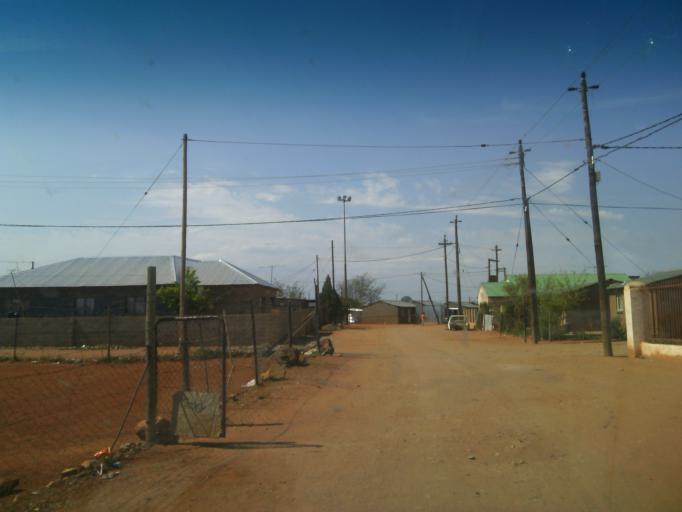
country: ZA
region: Northern Cape
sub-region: Frances Baard District Municipality
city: Barkly West
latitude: -28.5189
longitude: 24.5031
